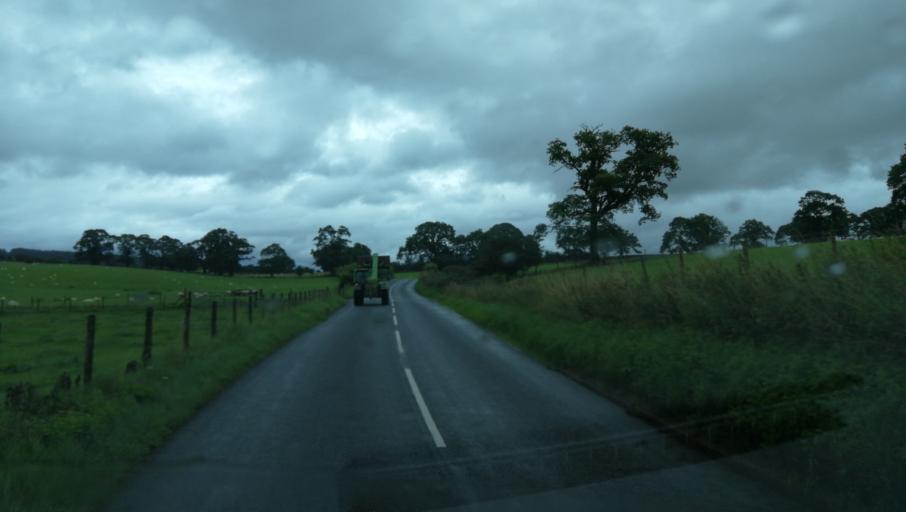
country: GB
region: England
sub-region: Cumbria
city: Penrith
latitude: 54.6170
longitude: -2.8289
